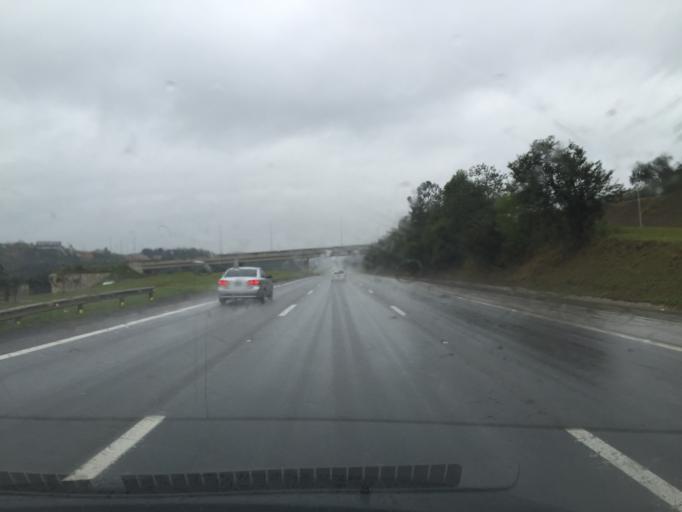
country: BR
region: Sao Paulo
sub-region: Mairinque
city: Mairinque
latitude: -23.4191
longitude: -47.2097
